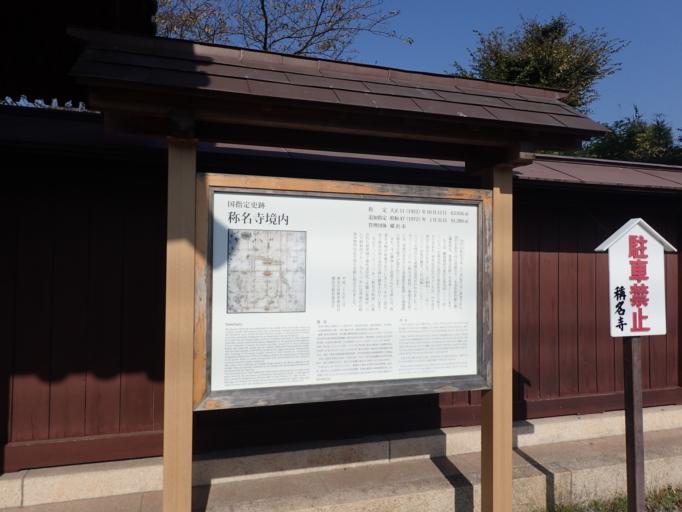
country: JP
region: Kanagawa
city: Yokosuka
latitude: 35.3419
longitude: 139.6295
